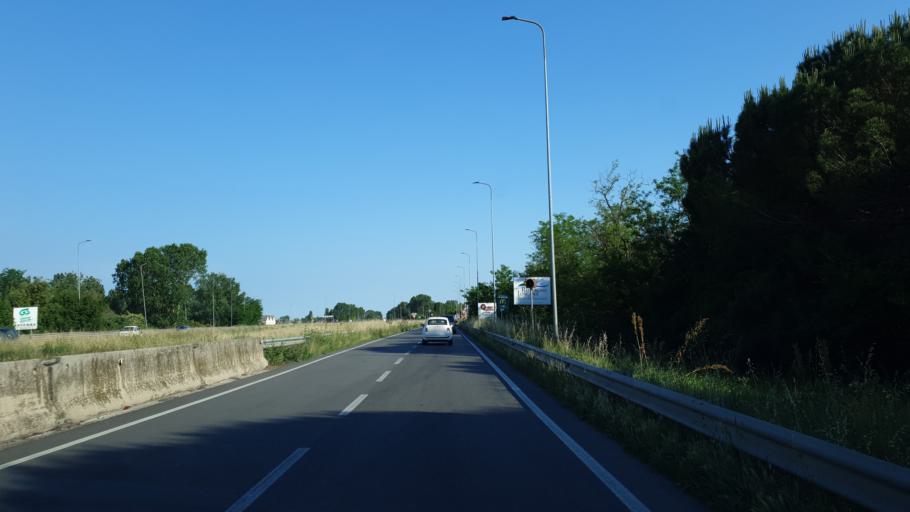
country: IT
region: Emilia-Romagna
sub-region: Provincia di Ravenna
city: Fosso Ghiaia
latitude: 44.3367
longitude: 12.2695
